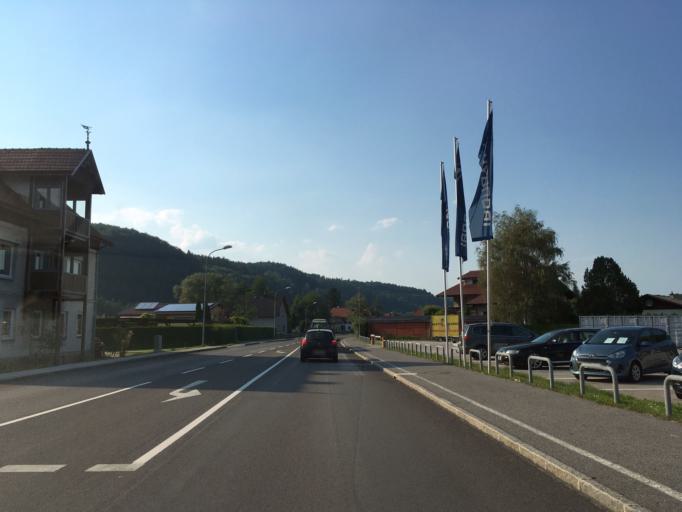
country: AT
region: Lower Austria
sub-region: Politischer Bezirk Neunkirchen
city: Grimmenstein
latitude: 47.6363
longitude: 16.1312
